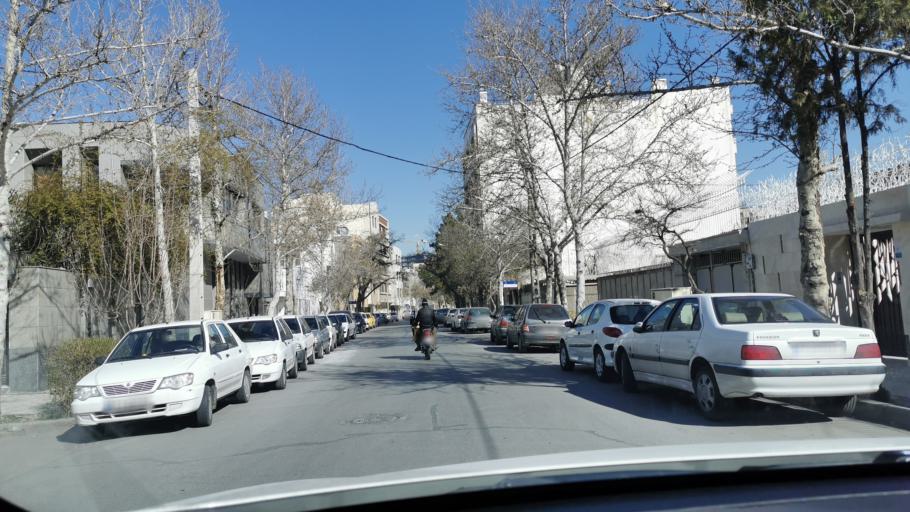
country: IR
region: Razavi Khorasan
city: Mashhad
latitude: 36.2894
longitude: 59.5772
